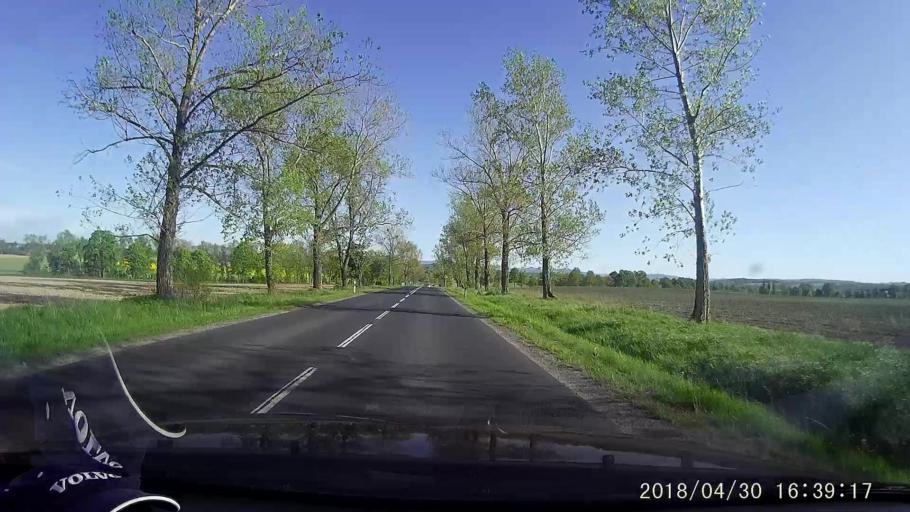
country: PL
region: Silesian Voivodeship
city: Zawidow
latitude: 51.0432
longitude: 15.0452
